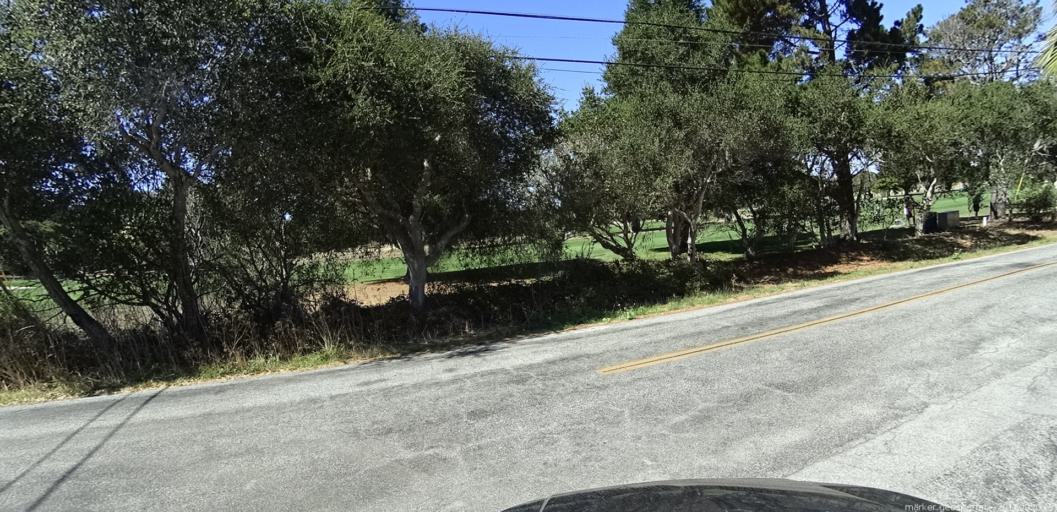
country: US
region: California
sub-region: Monterey County
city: Monterey
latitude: 36.5793
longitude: -121.8687
